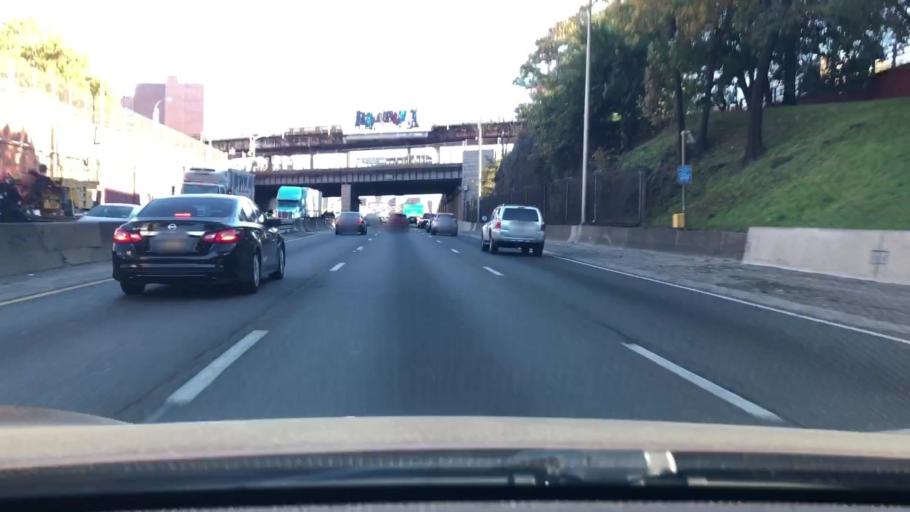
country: US
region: New York
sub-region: Bronx
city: The Bronx
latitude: 40.8401
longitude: -73.8855
